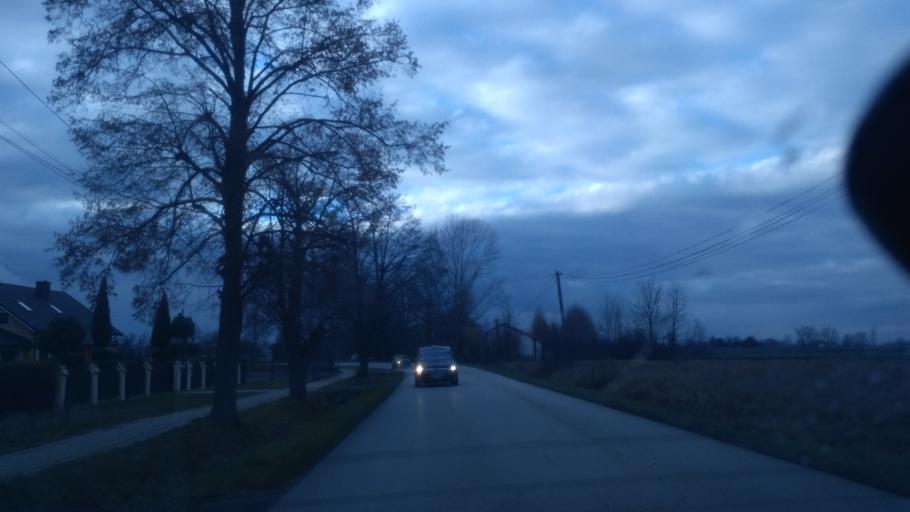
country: PL
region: Subcarpathian Voivodeship
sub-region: Powiat lancucki
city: Gluchow
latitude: 50.1002
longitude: 22.2697
